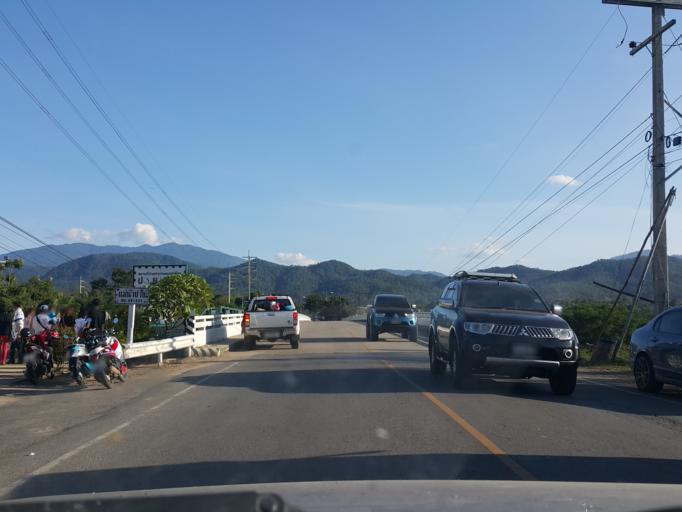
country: TH
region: Mae Hong Son
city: Mae Hi
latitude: 19.2988
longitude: 98.4642
